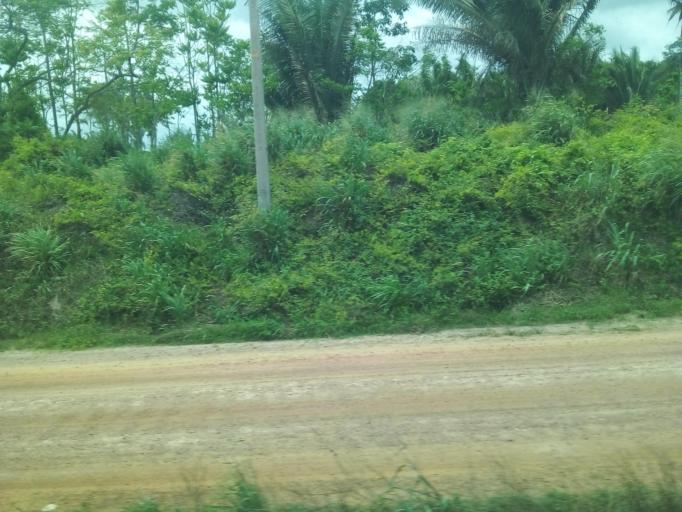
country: BR
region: Maranhao
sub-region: Santa Ines
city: Santa Ines
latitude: -3.6593
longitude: -45.8283
